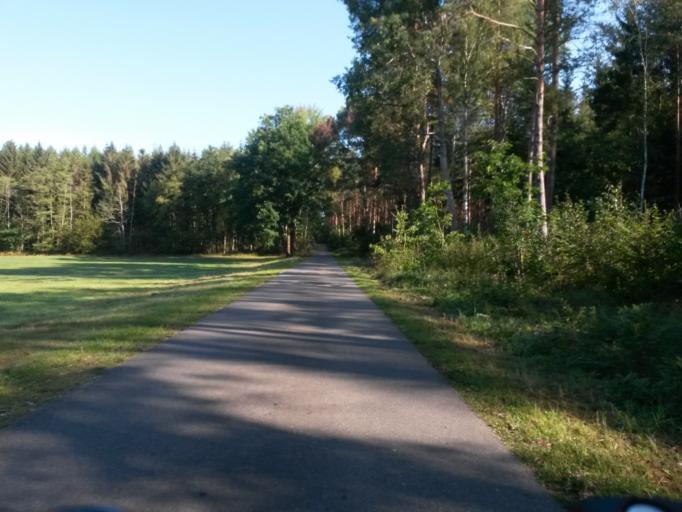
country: DE
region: Brandenburg
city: Templin
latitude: 53.1470
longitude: 13.4338
